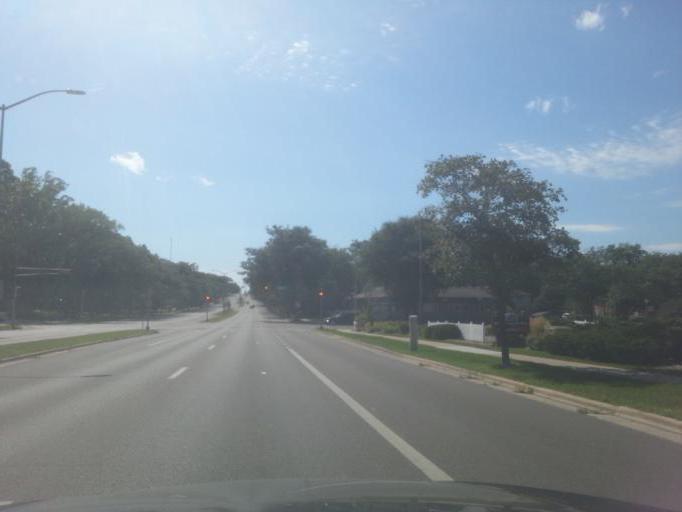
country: US
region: Wisconsin
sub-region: Dane County
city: Middleton
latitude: 43.0609
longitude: -89.4856
